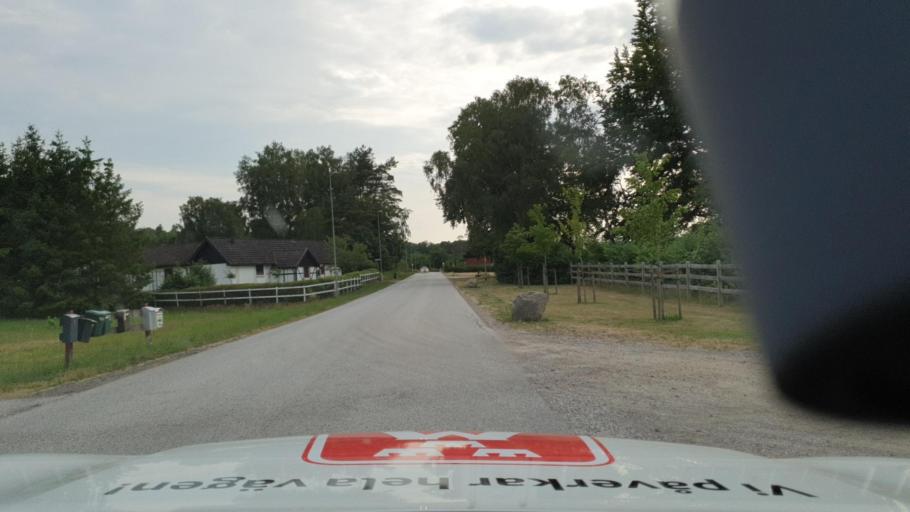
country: SE
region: Skane
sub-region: Sjobo Kommun
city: Sjoebo
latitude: 55.6304
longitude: 13.7268
